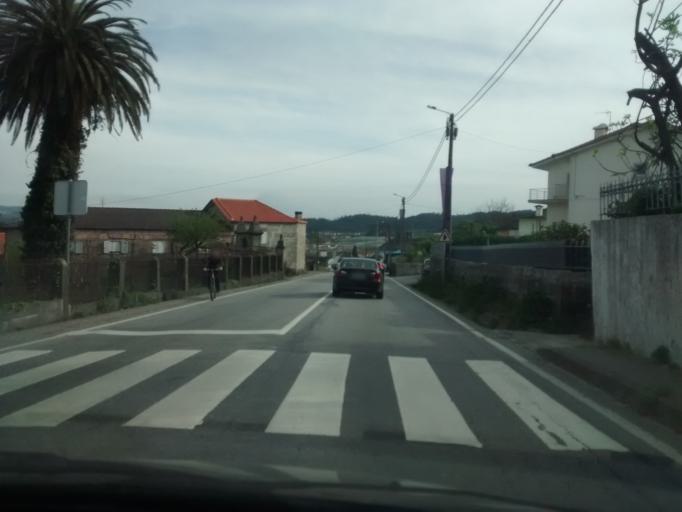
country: PT
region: Braga
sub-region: Guimaraes
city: Brito
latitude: 41.4998
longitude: -8.3649
